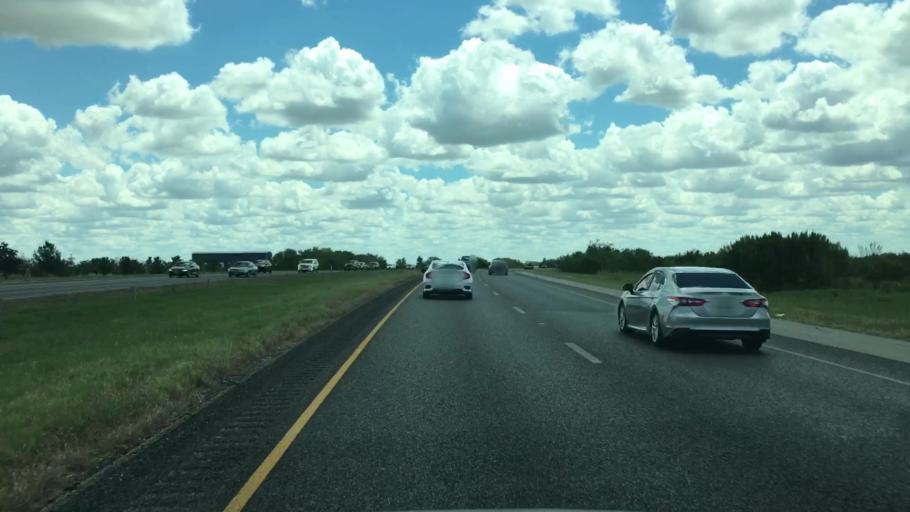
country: US
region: Texas
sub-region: Bexar County
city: Elmendorf
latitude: 29.3039
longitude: -98.3969
